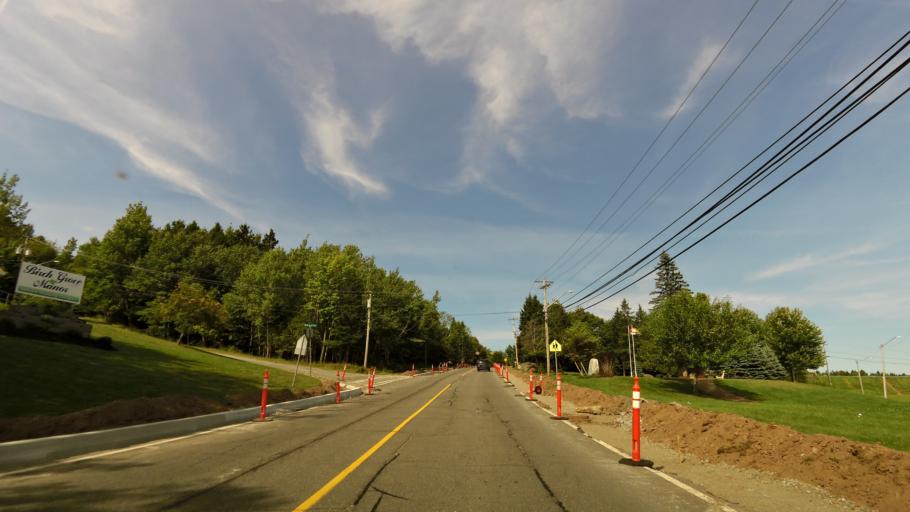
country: CA
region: New Brunswick
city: Hampton
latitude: 45.5314
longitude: -65.8319
